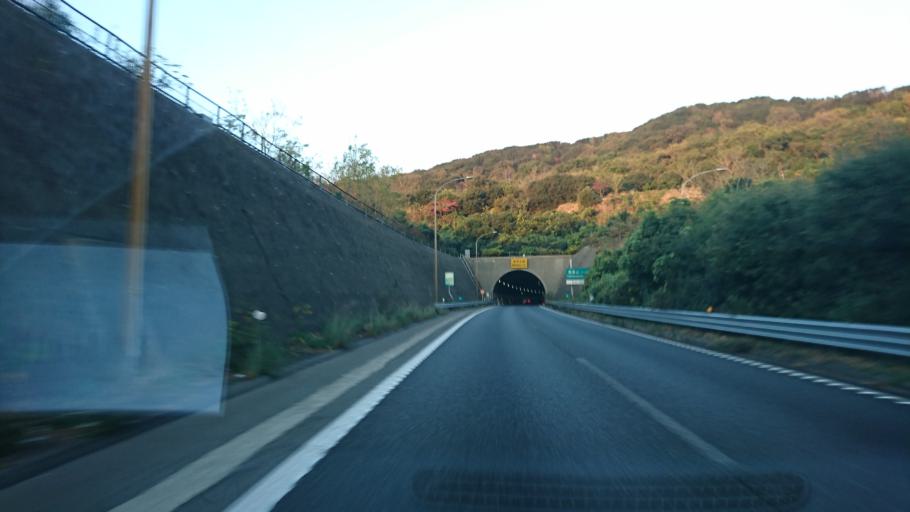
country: JP
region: Hyogo
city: Kobe
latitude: 34.6500
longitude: 135.1039
